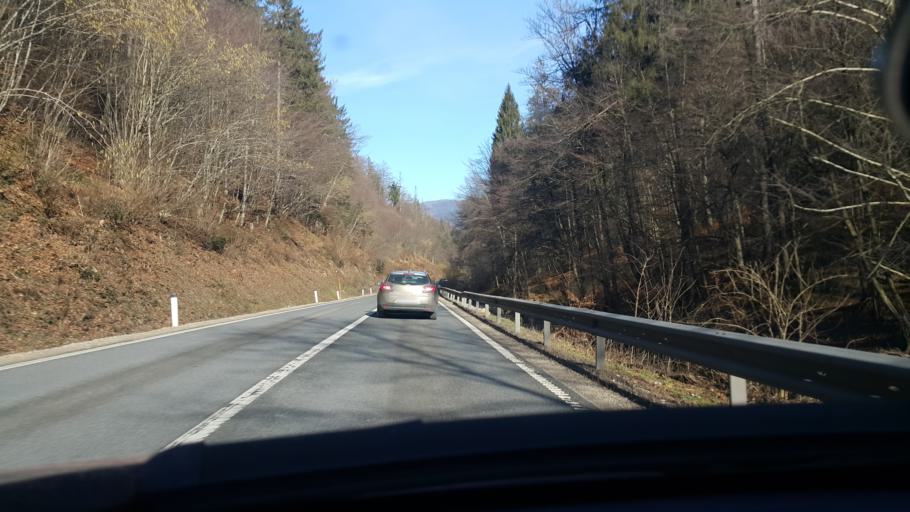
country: SI
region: Zalec
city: Gotovlje
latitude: 46.3094
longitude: 15.1734
